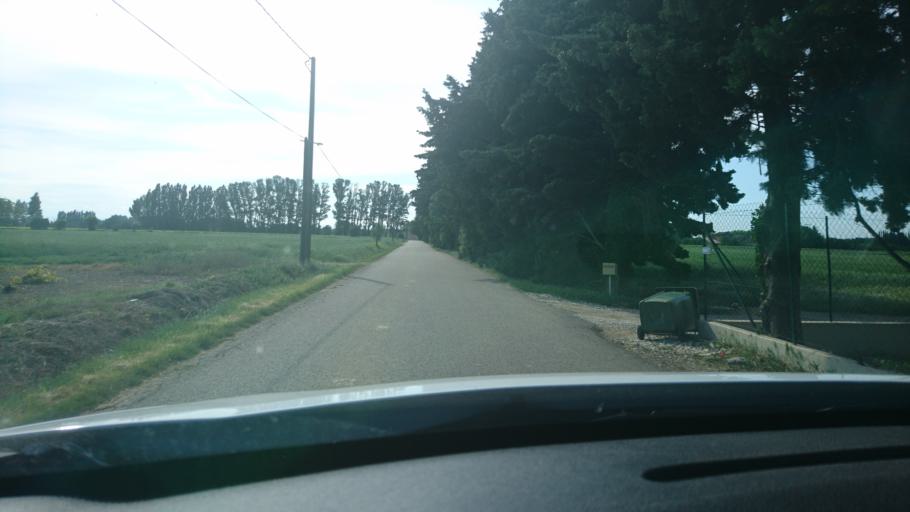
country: FR
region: Provence-Alpes-Cote d'Azur
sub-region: Departement du Vaucluse
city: Jonquieres
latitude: 44.1316
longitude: 4.8866
